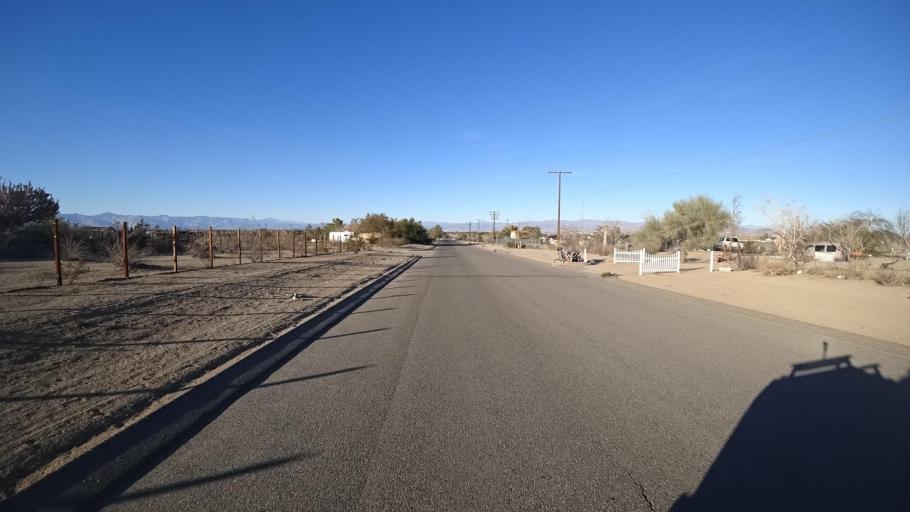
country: US
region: California
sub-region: Kern County
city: Ridgecrest
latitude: 35.5893
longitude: -117.6616
